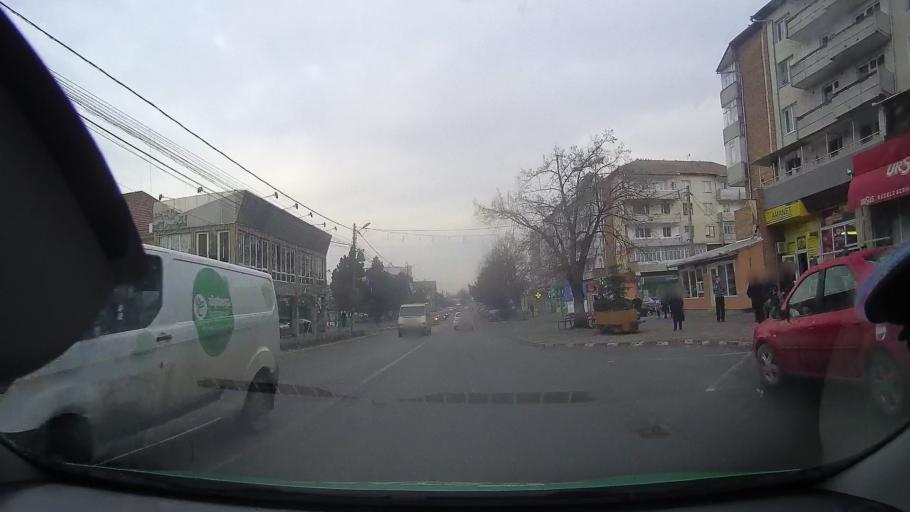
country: RO
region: Mures
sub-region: Comuna Ludus
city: Ludus
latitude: 46.4757
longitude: 24.0955
